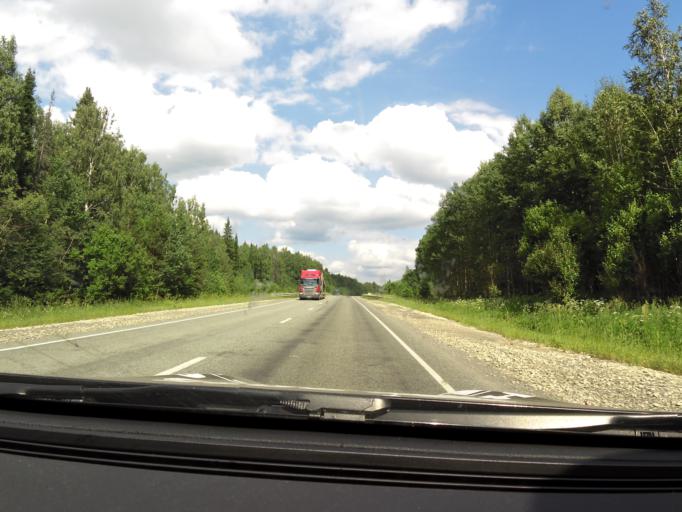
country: RU
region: Sverdlovsk
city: Bisert'
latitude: 56.8288
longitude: 59.1162
